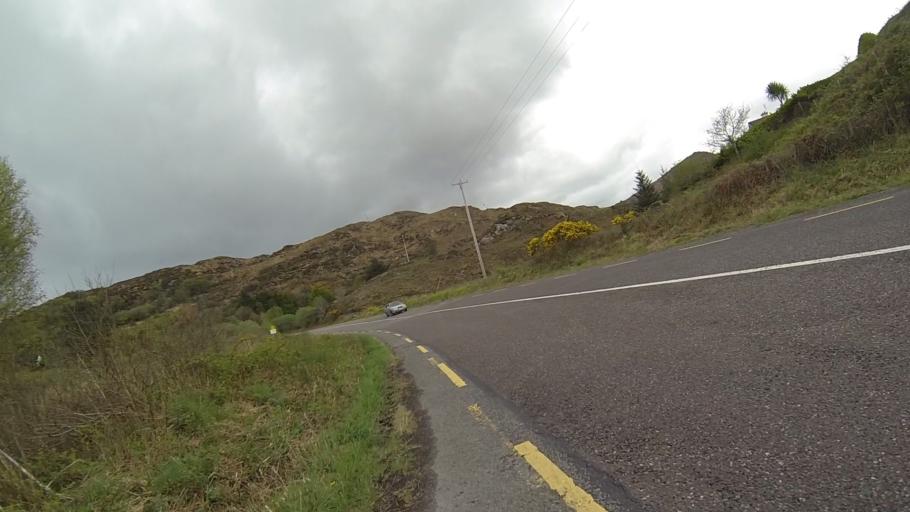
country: IE
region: Munster
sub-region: County Cork
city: Bantry
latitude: 51.7219
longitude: -9.5794
